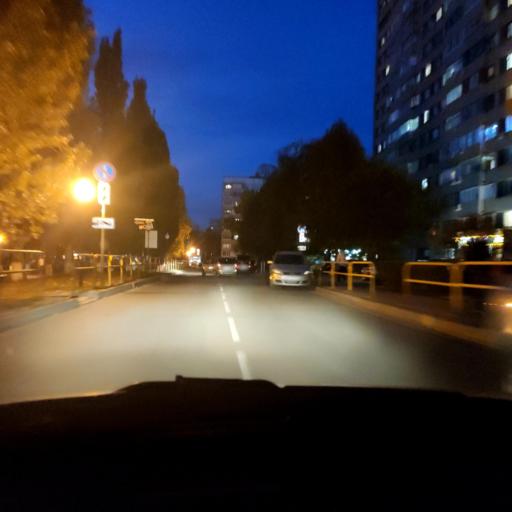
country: RU
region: Samara
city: Tol'yatti
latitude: 53.5284
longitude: 49.3198
